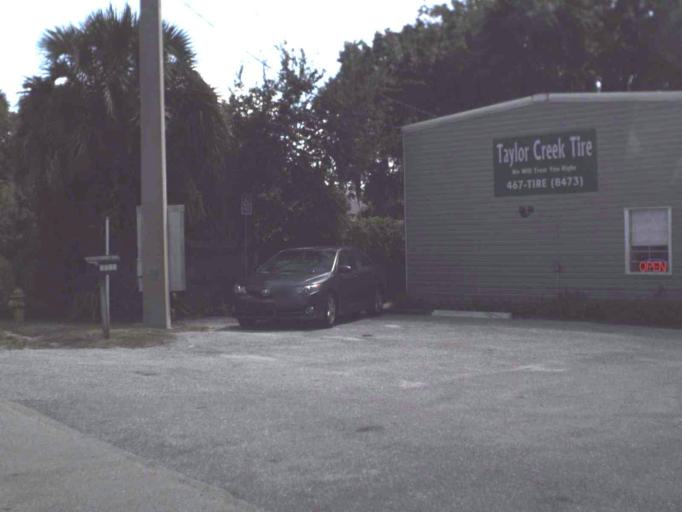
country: US
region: Florida
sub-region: Okeechobee County
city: Taylor Creek
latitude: 27.2094
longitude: -80.7900
